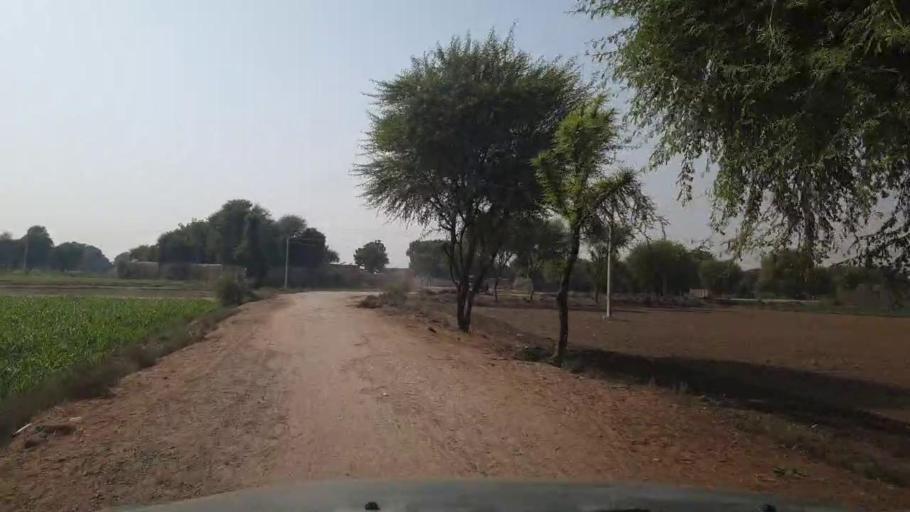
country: PK
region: Sindh
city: Bhit Shah
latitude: 25.7363
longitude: 68.5059
